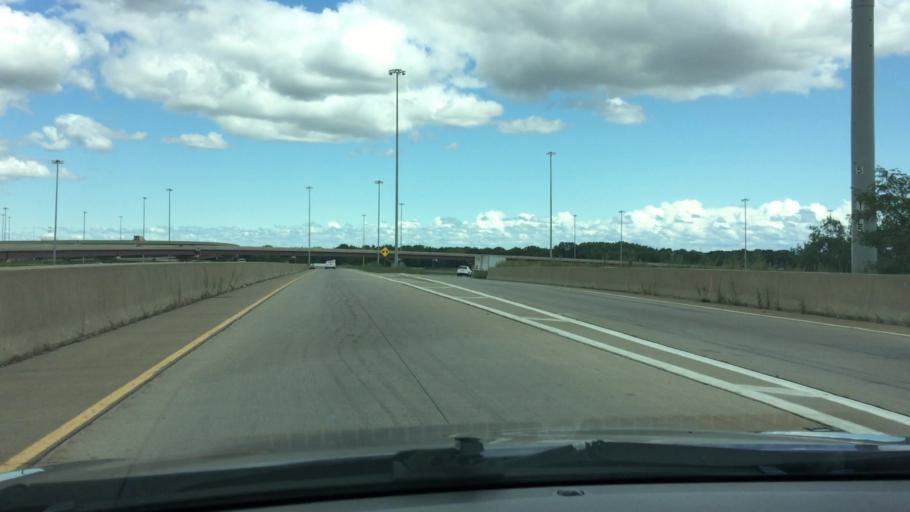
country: US
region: Illinois
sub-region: Cook County
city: Thornton
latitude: 41.5749
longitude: -87.5826
